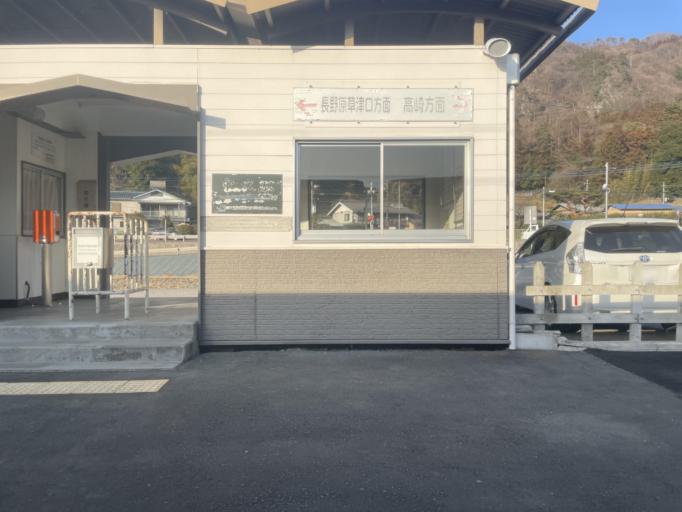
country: JP
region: Gunma
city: Nakanojomachi
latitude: 36.5708
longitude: 138.8822
